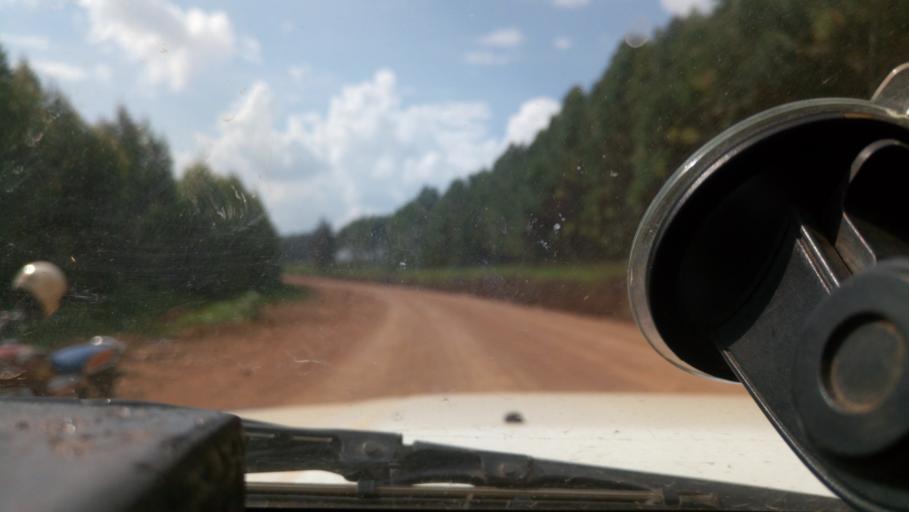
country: KE
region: Nyamira District
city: Nyamira
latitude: -0.5802
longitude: 35.0509
